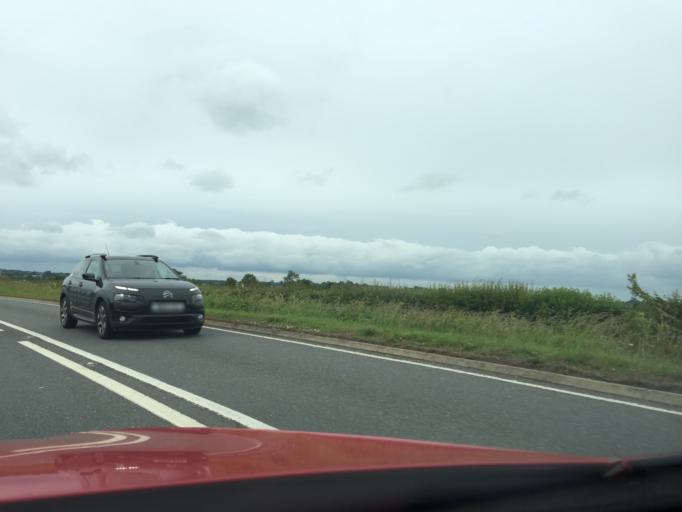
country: GB
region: England
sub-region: Warwickshire
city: Southam
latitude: 52.2541
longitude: -1.3416
